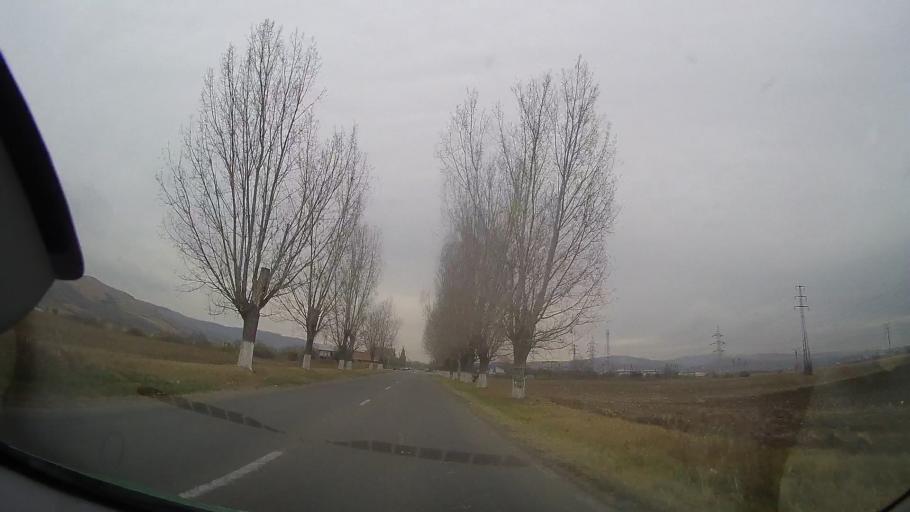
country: RO
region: Prahova
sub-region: Oras Urlati
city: Urlati
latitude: 44.9700
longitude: 26.2338
